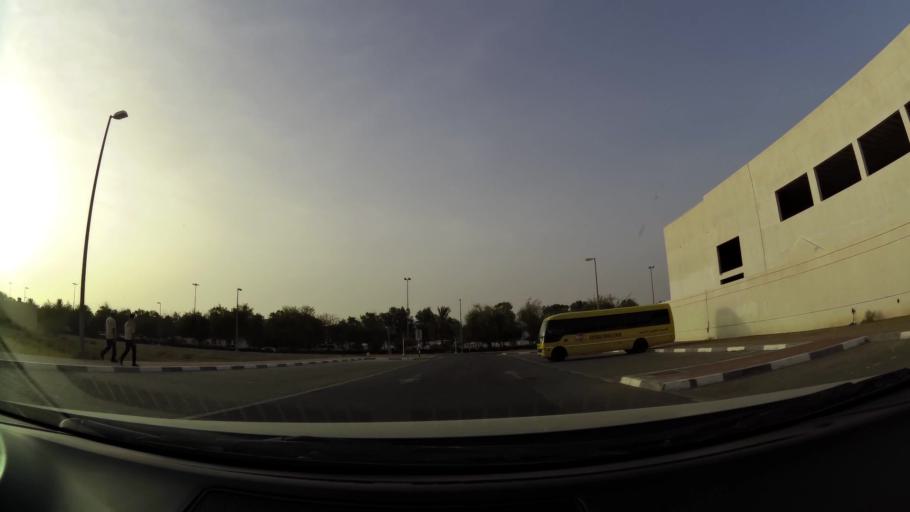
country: AE
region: Abu Dhabi
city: Al Ain
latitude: 24.2470
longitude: 55.7238
